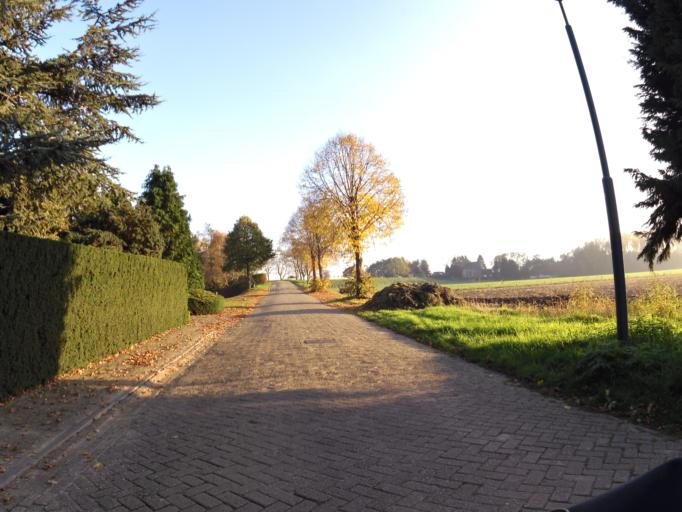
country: NL
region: Gelderland
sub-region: Gemeente Zaltbommel
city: Nederhemert-Noord
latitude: 51.7316
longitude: 5.1887
